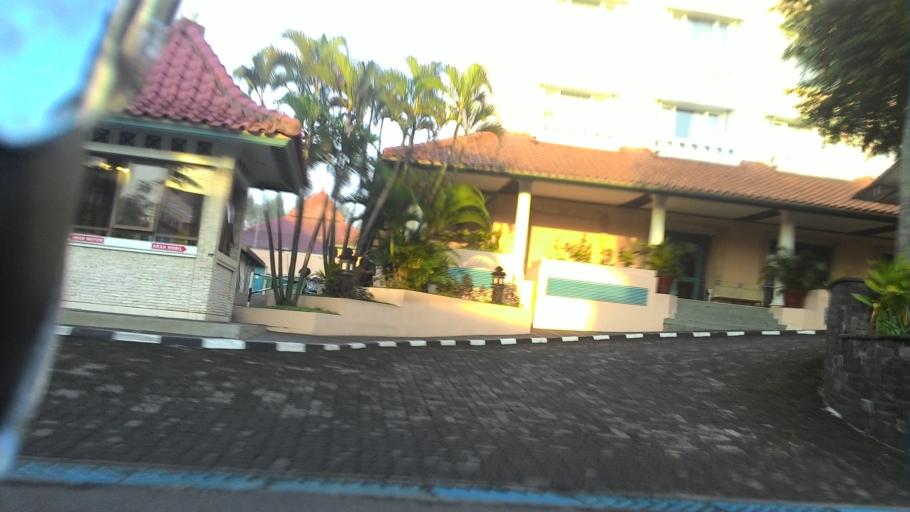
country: ID
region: Daerah Istimewa Yogyakarta
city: Yogyakarta
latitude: -7.7978
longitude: 110.3694
